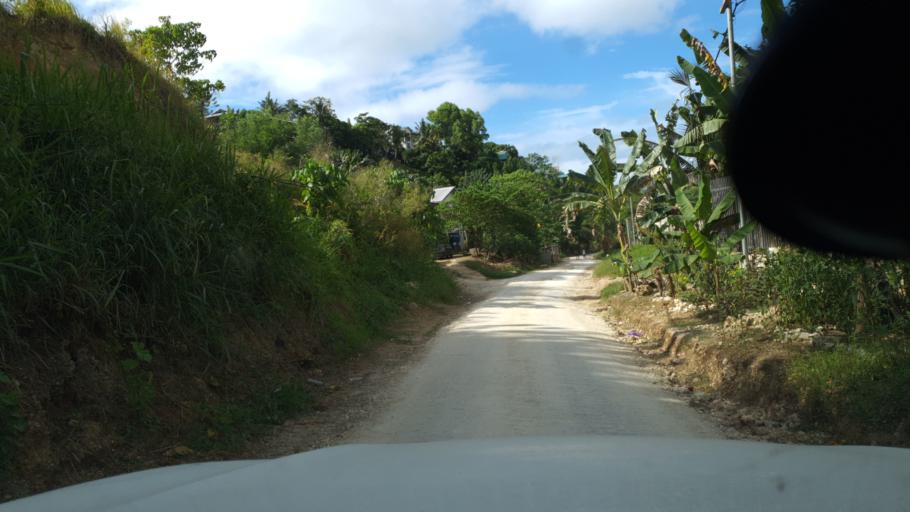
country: SB
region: Guadalcanal
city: Honiara
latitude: -9.4362
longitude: 159.9303
